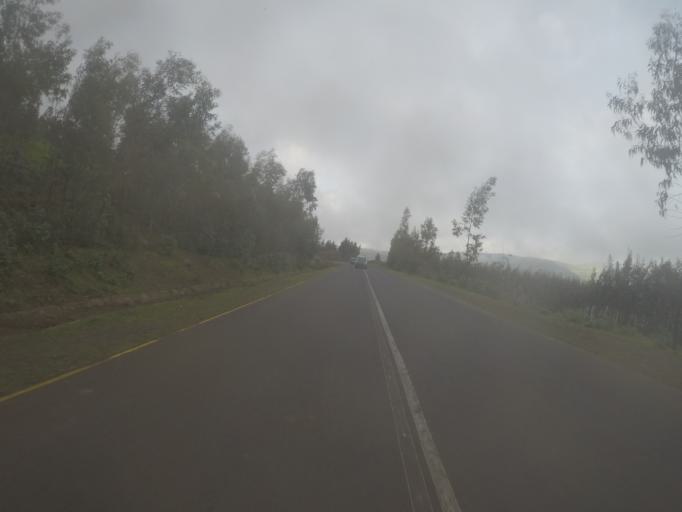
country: ET
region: Amhara
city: Gondar
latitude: 12.7295
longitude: 37.5146
